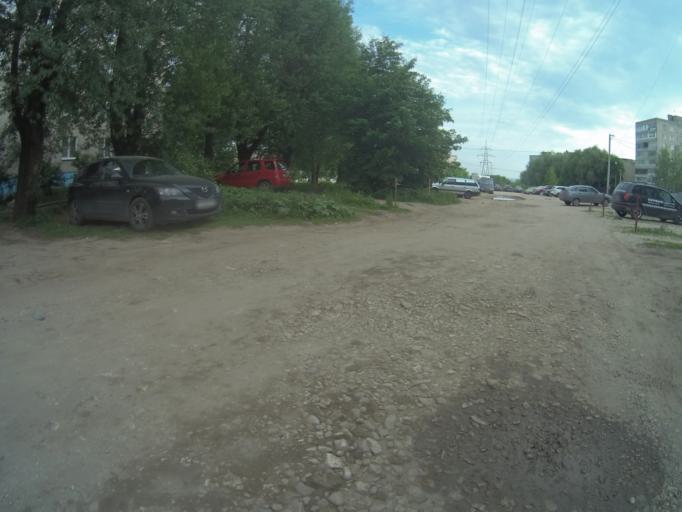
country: RU
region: Vladimir
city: Kommunar
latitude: 56.1635
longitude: 40.4518
